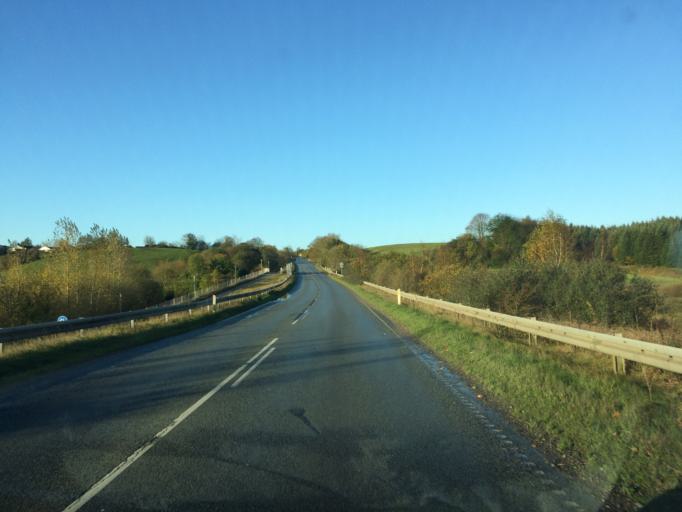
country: DK
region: South Denmark
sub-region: Kolding Kommune
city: Kolding
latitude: 55.5129
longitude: 9.5224
